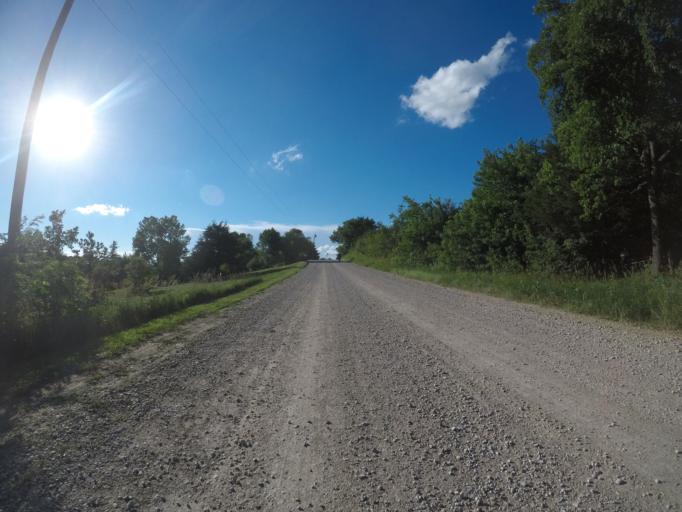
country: US
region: Kansas
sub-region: Riley County
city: Ogden
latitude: 39.2348
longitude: -96.7260
